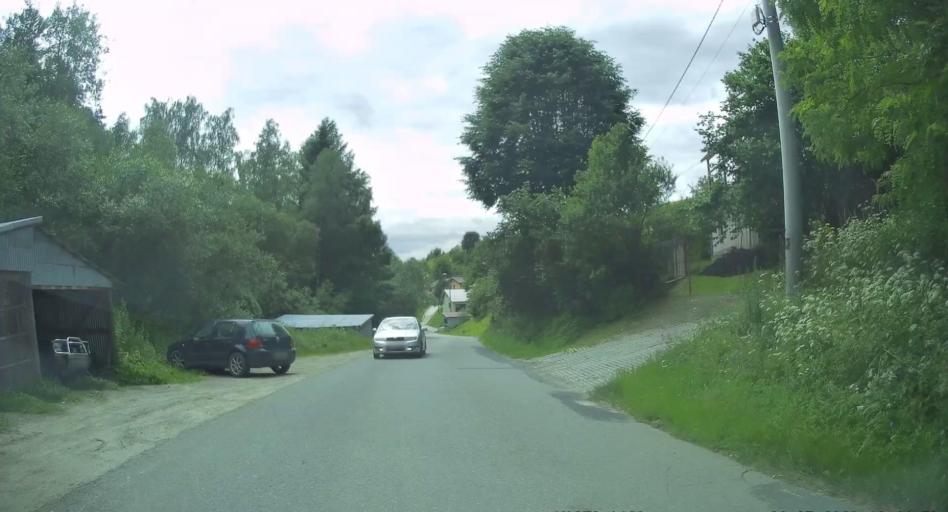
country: PL
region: Lesser Poland Voivodeship
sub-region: Powiat nowosadecki
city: Muszyna
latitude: 49.3827
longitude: 20.8976
